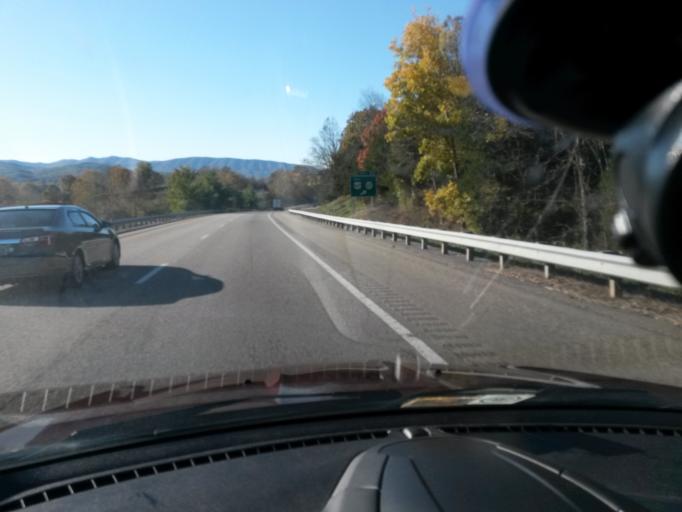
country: US
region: Virginia
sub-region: City of Lexington
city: Lexington
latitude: 37.8490
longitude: -79.4717
